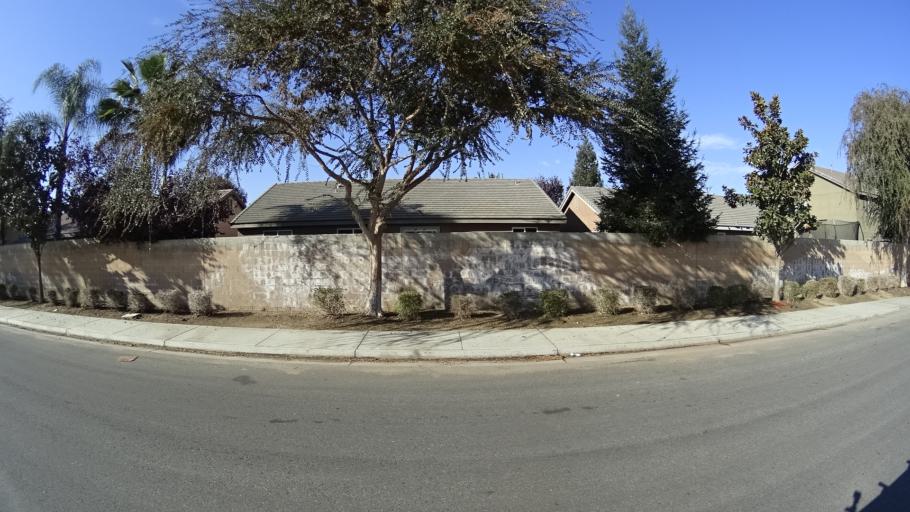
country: US
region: California
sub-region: Kern County
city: Greenfield
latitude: 35.2680
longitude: -119.0656
